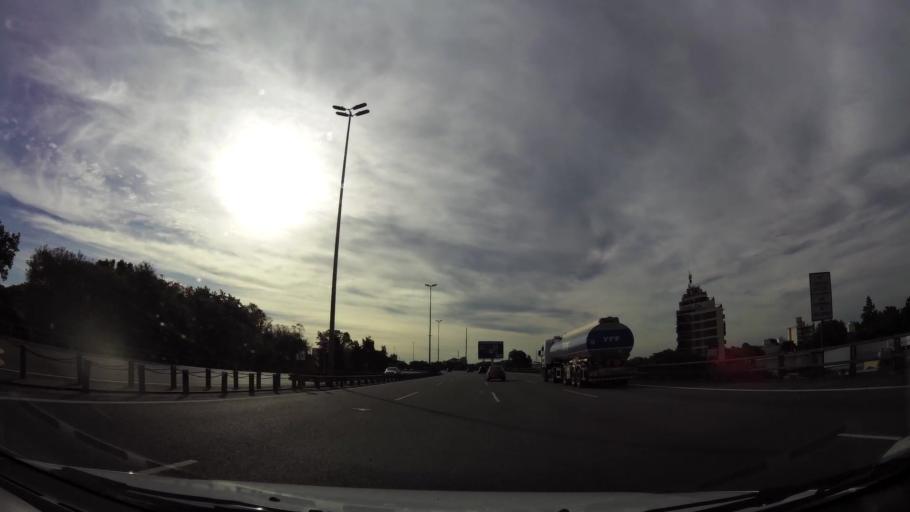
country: AR
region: Buenos Aires F.D.
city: Villa Santa Rita
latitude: -34.6357
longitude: -58.5093
